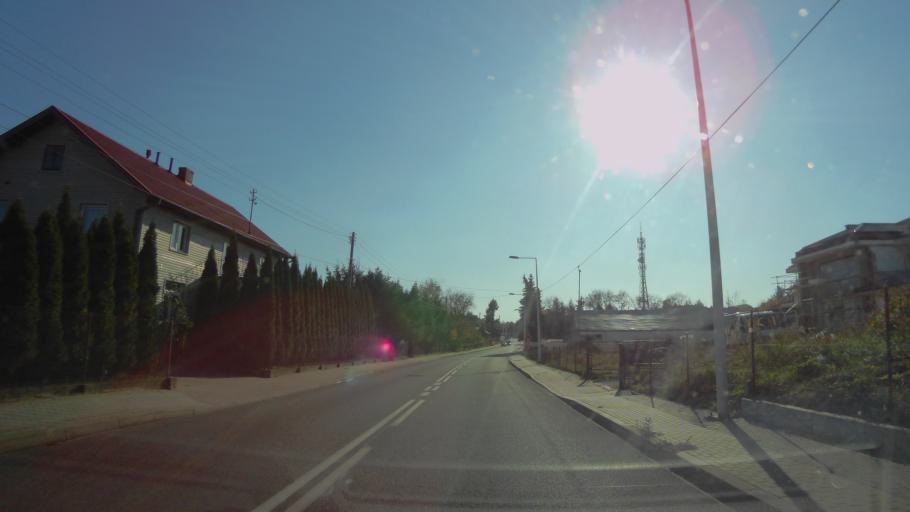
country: PL
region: Subcarpathian Voivodeship
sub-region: Powiat lezajski
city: Lezajsk
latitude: 50.2615
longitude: 22.4236
